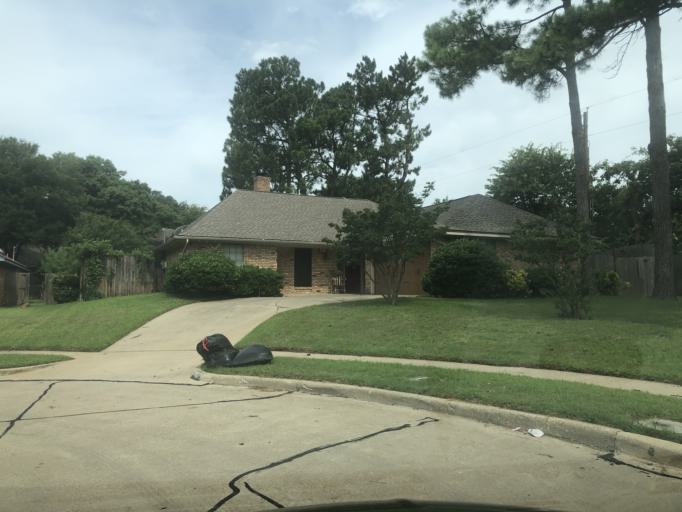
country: US
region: Texas
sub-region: Dallas County
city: Irving
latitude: 32.7978
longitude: -96.9817
